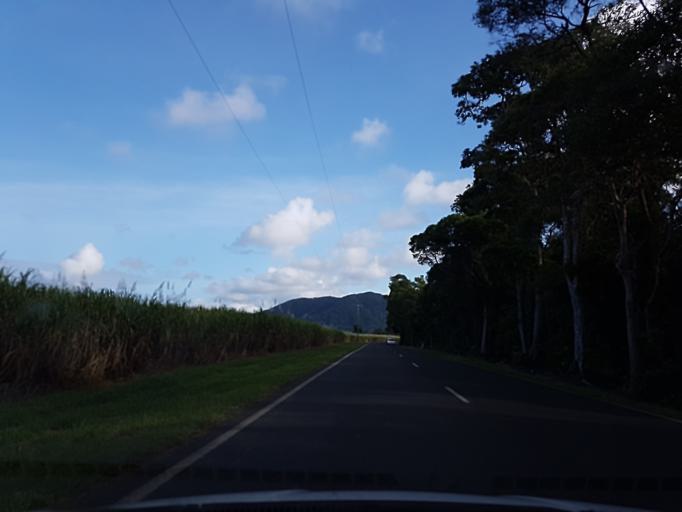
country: AU
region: Queensland
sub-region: Cairns
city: Port Douglas
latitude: -16.2725
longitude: 145.3914
